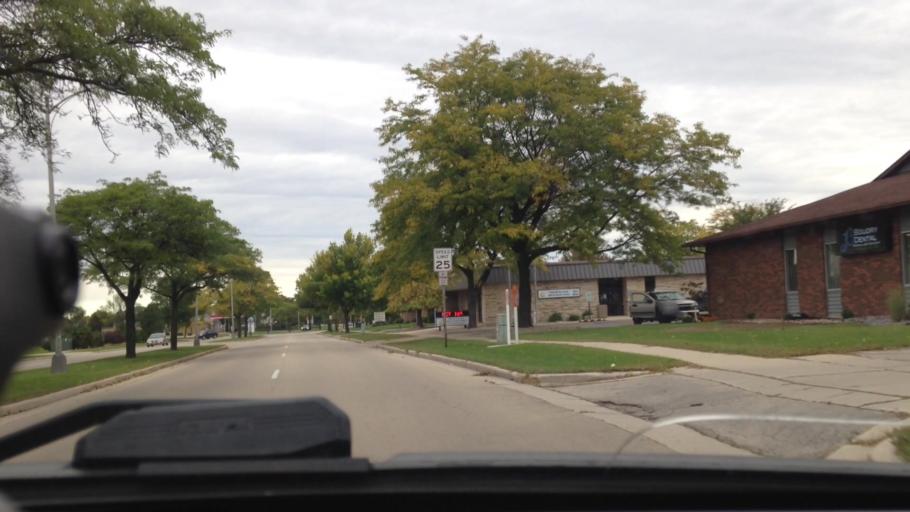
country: US
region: Wisconsin
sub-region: Fond du Lac County
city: North Fond du Lac
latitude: 43.7862
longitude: -88.4728
